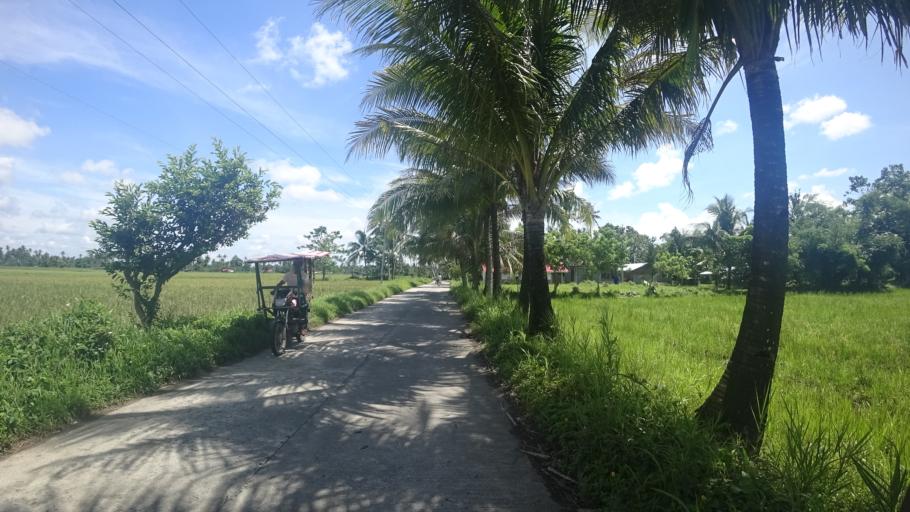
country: PH
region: Eastern Visayas
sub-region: Province of Leyte
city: Alangalang
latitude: 11.2269
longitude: 124.8459
